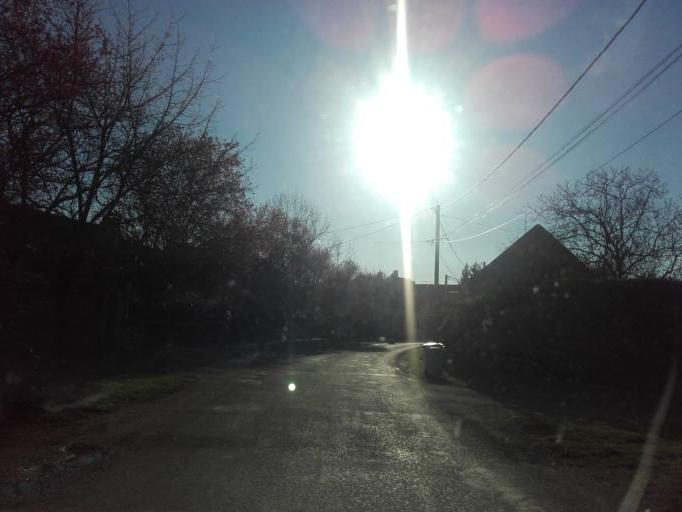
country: FR
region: Bourgogne
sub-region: Departement de Saone-et-Loire
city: Demigny
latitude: 46.9369
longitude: 4.8033
